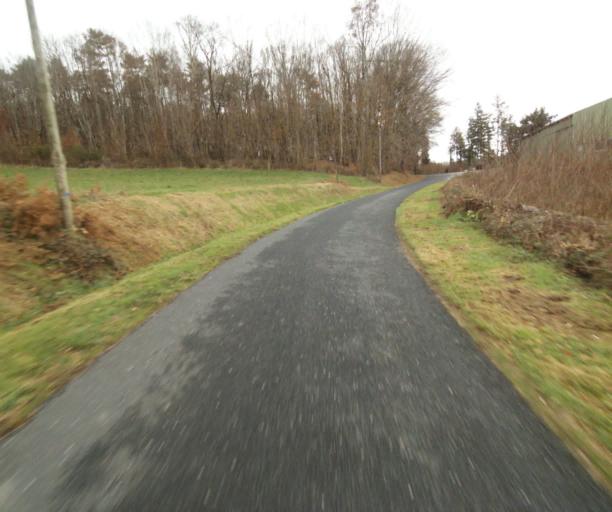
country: FR
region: Limousin
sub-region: Departement de la Correze
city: Saint-Mexant
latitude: 45.3033
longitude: 1.6406
